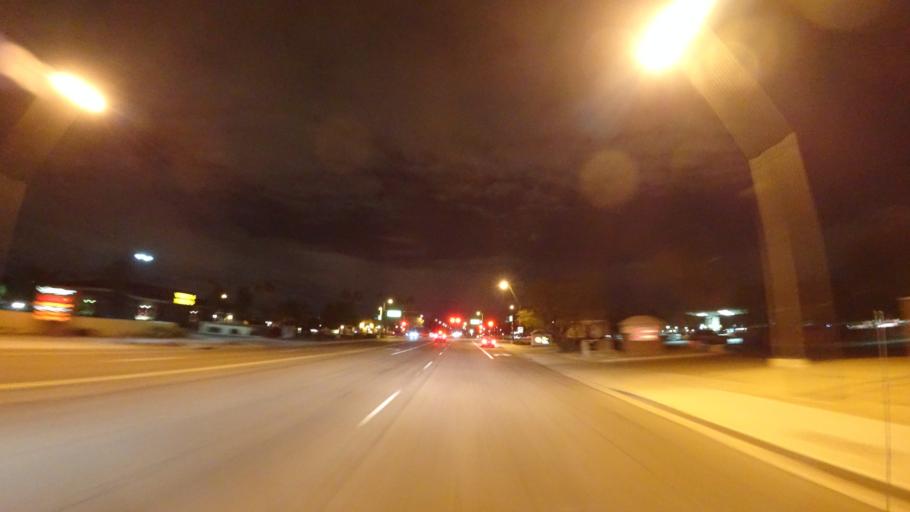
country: US
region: Arizona
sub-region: Maricopa County
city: San Carlos
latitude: 33.3336
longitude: -111.9111
